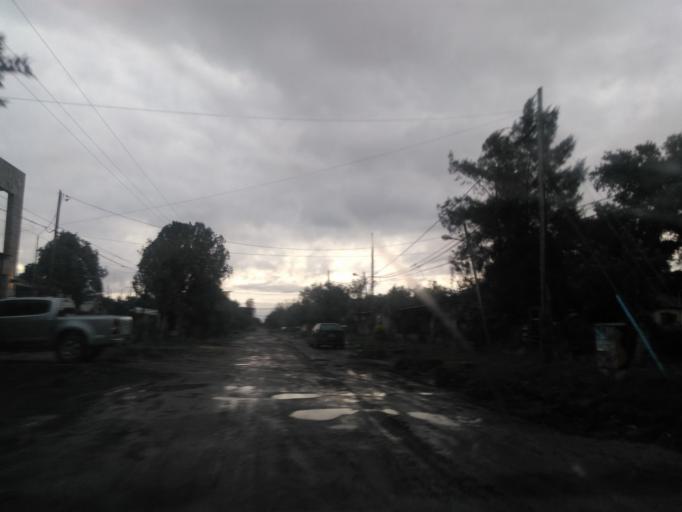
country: AR
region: Chaco
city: Resistencia
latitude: -27.4672
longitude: -59.0009
